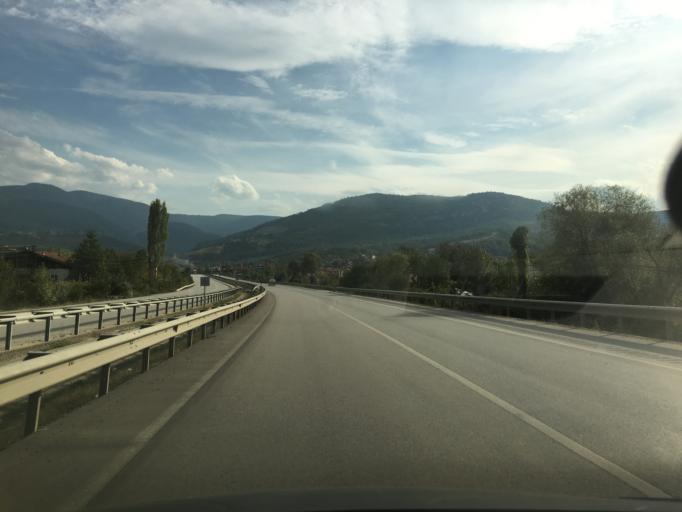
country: TR
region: Karabuk
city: Karabuk
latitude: 41.1096
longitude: 32.6687
